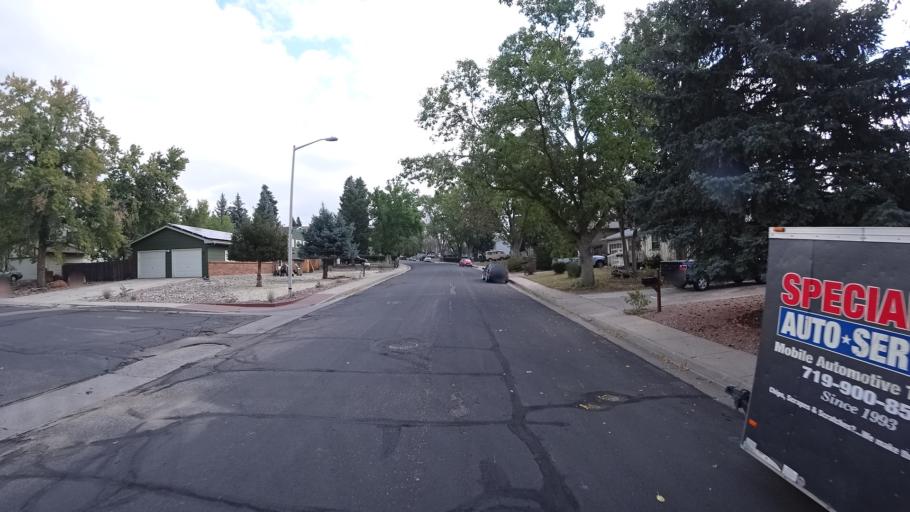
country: US
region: Colorado
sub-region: El Paso County
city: Cimarron Hills
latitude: 38.8797
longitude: -104.7427
